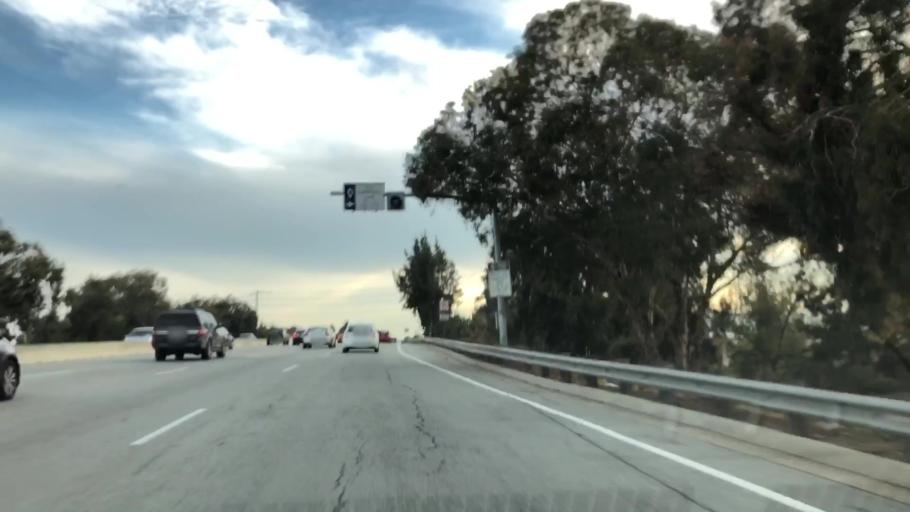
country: US
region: California
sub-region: Santa Clara County
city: Santa Clara
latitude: 37.3680
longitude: -121.9655
